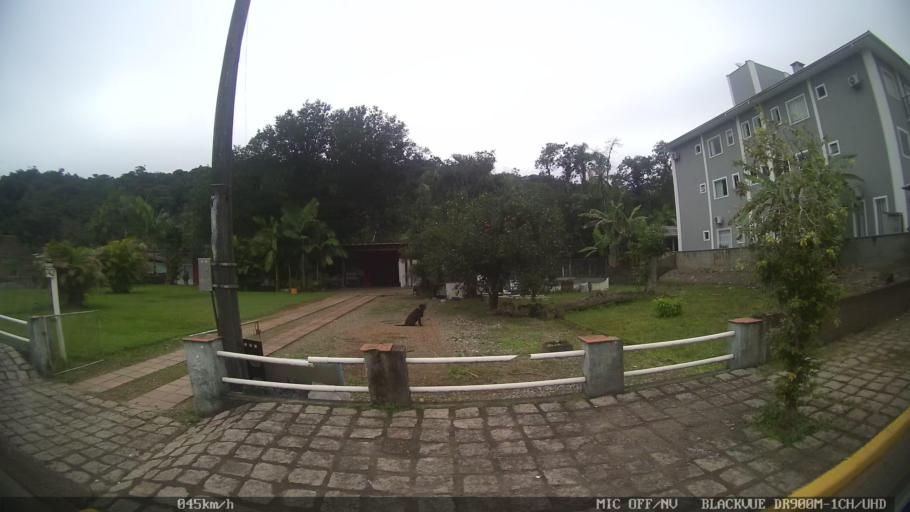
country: BR
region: Santa Catarina
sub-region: Joinville
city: Joinville
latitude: -26.2151
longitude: -48.9120
